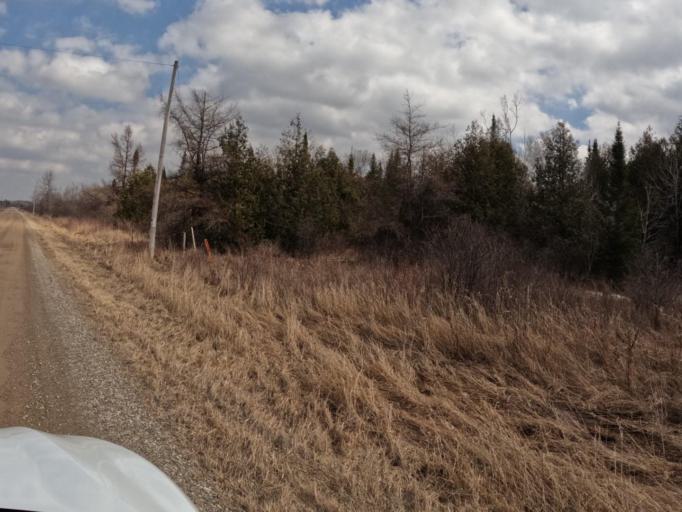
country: CA
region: Ontario
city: Shelburne
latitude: 44.0193
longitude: -80.3033
